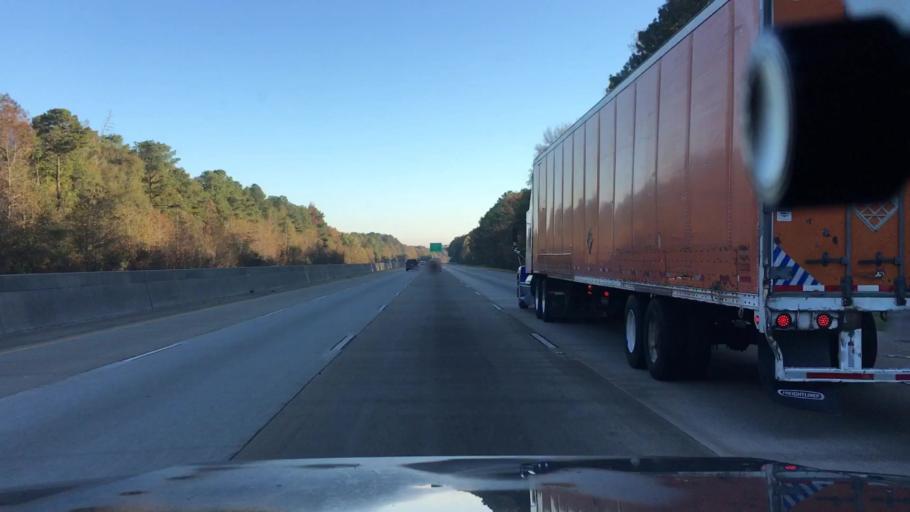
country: US
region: Georgia
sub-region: Fulton County
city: Palmetto
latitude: 33.4827
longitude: -84.6555
